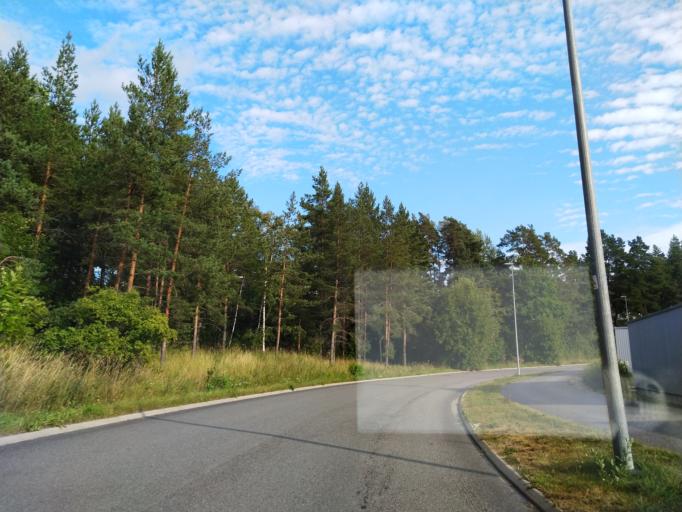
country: FI
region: Varsinais-Suomi
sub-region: Turku
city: Turku
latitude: 60.4258
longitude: 22.2072
